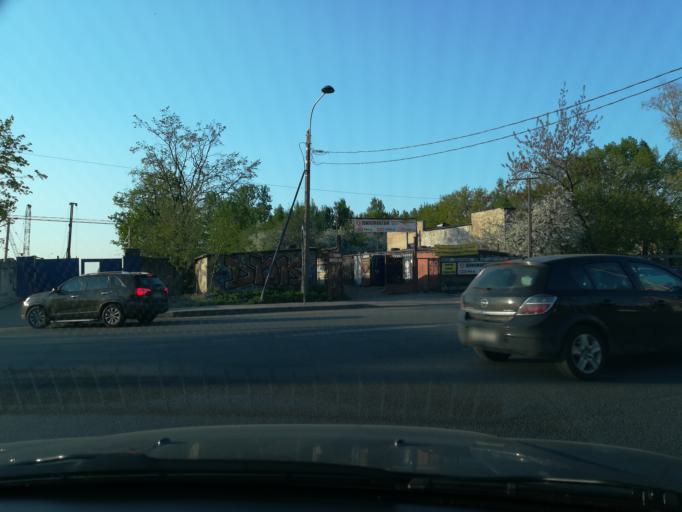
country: RU
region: St.-Petersburg
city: Vasyl'evsky Ostrov
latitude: 59.9559
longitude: 30.2474
